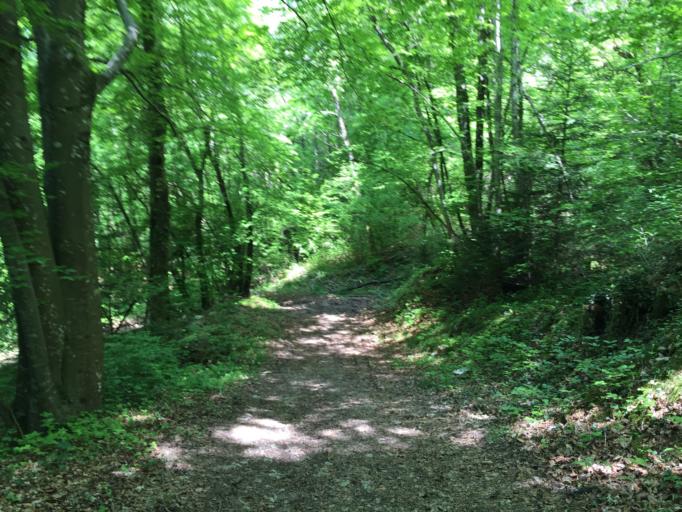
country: FR
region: Rhone-Alpes
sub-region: Departement de la Savoie
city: Mery
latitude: 45.6571
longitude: 5.9525
